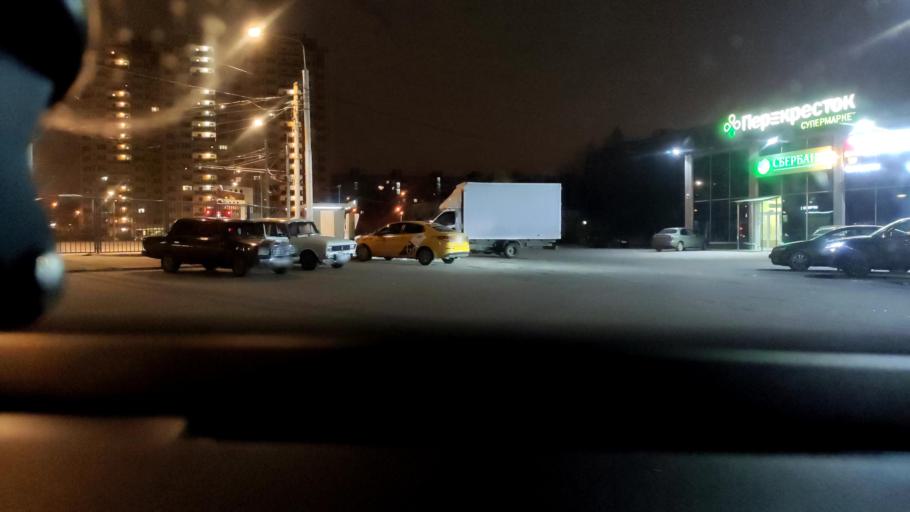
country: RU
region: Moscow
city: Gol'yanovo
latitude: 55.8225
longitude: 37.8243
